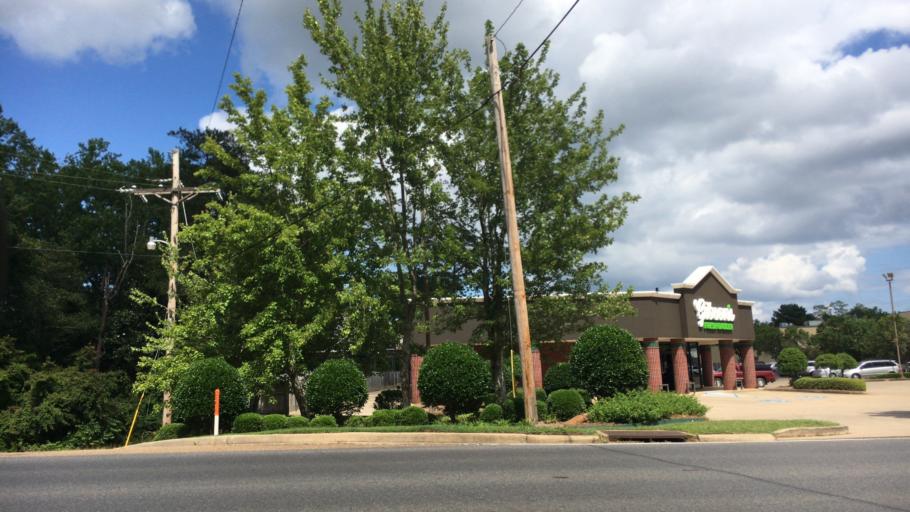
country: US
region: Louisiana
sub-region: Lincoln Parish
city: Ruston
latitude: 32.5458
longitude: -92.6397
